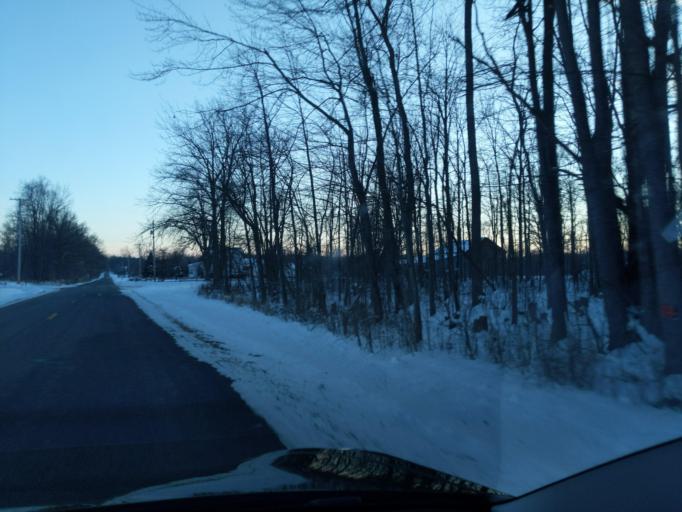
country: US
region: Michigan
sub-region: Ingham County
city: Williamston
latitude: 42.5710
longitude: -84.3180
